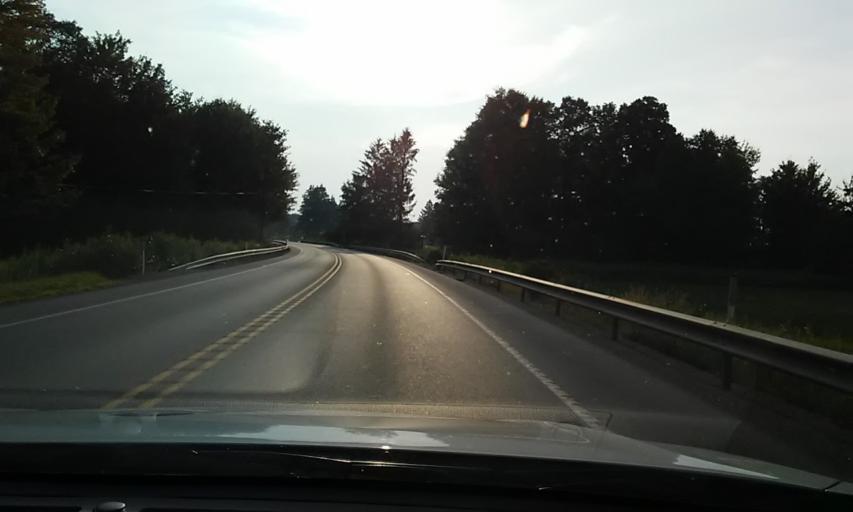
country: US
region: Pennsylvania
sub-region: McKean County
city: Kane
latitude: 41.6737
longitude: -78.7592
